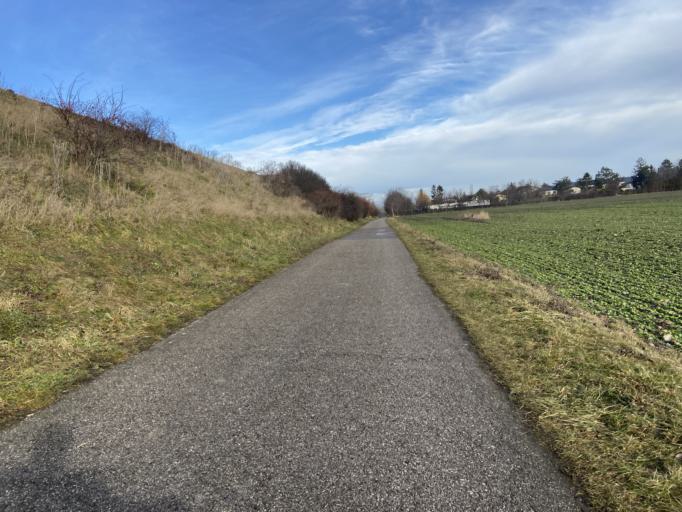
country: AT
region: Lower Austria
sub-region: Politischer Bezirk Modling
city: Laxenburg
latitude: 48.0676
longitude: 16.3447
